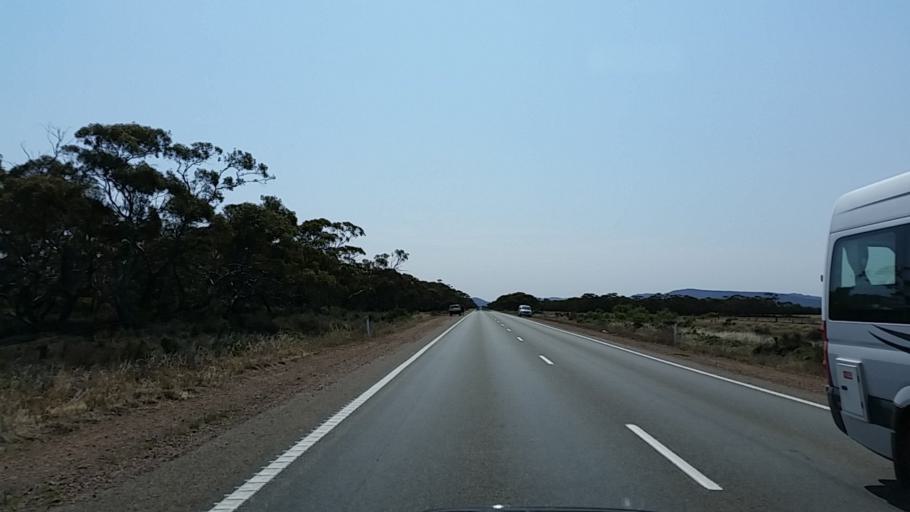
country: AU
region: South Australia
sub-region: Port Pirie City and Dists
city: Port Pirie
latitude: -32.9424
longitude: 137.9824
